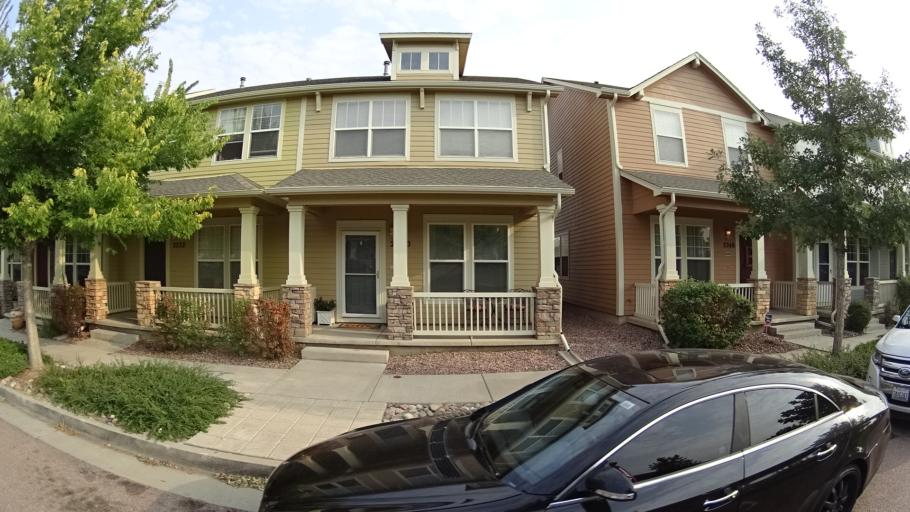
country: US
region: Colorado
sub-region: El Paso County
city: Stratmoor
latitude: 38.8095
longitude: -104.7849
